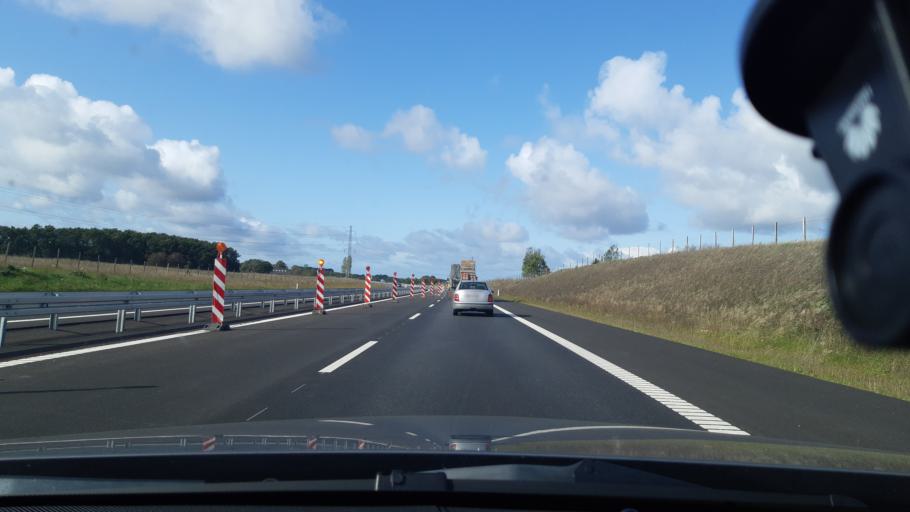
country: DK
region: Zealand
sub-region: Holbaek Kommune
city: Holbaek
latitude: 55.6603
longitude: 11.6144
